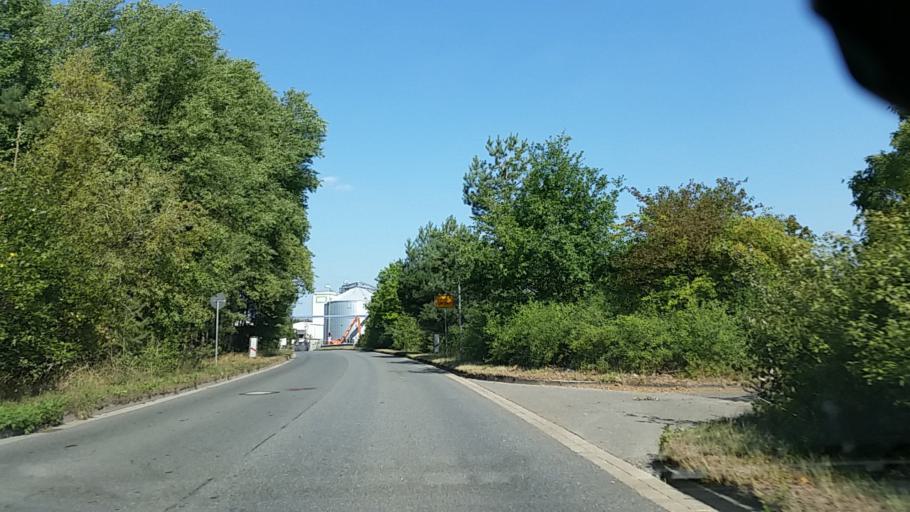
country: DE
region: Lower Saxony
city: Emmendorf
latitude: 52.9977
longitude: 10.5672
